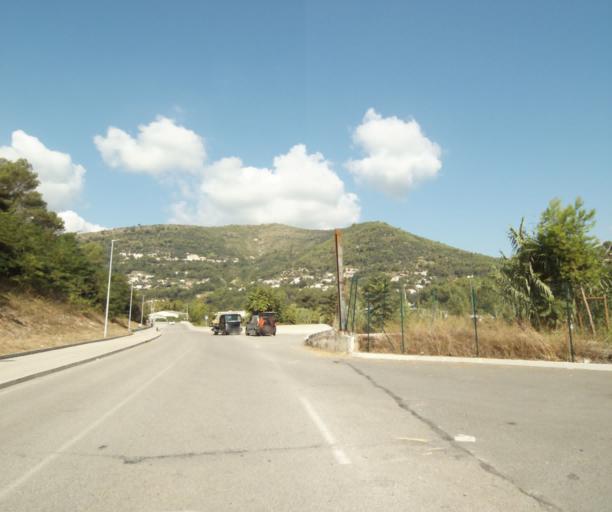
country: FR
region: Provence-Alpes-Cote d'Azur
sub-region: Departement des Alpes-Maritimes
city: Drap
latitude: 43.7649
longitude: 7.3345
